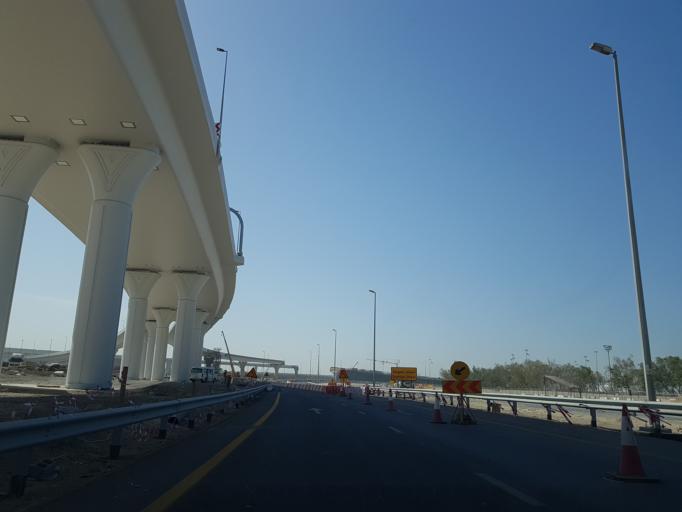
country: AE
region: Dubai
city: Dubai
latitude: 25.0182
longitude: 55.0945
